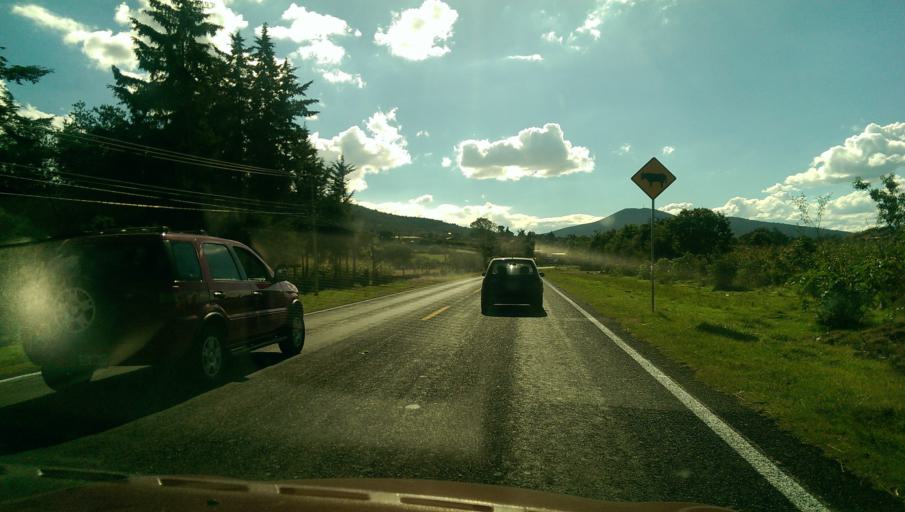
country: MX
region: Michoacan
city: Quiroga
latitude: 19.6409
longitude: -101.5381
